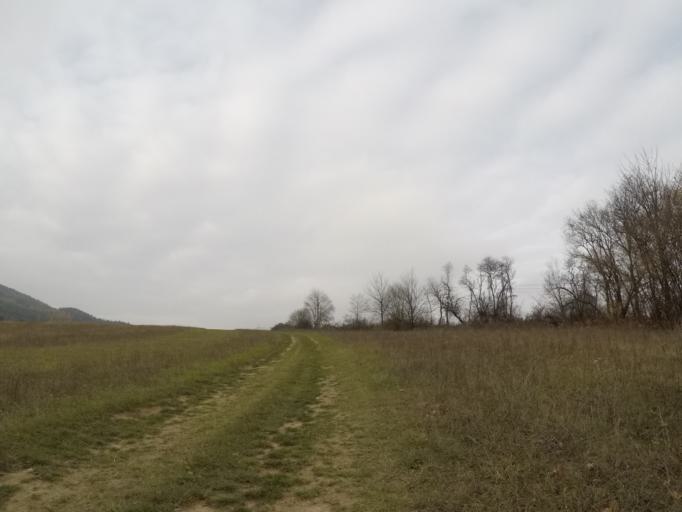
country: SK
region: Presovsky
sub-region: Okres Presov
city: Presov
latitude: 48.9030
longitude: 21.1838
